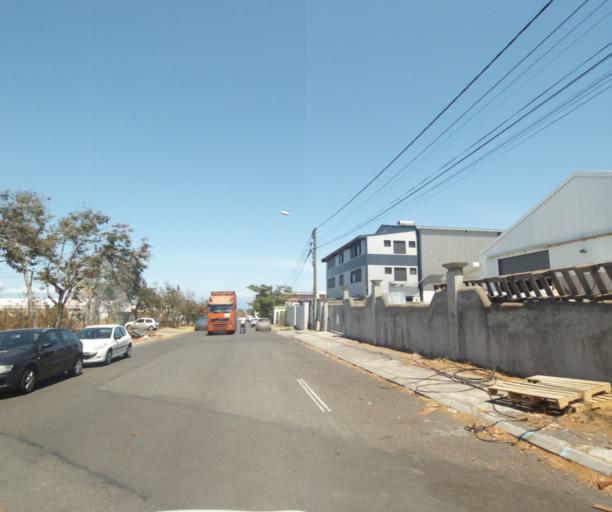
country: RE
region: Reunion
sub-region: Reunion
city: Le Port
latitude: -20.9627
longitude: 55.2970
